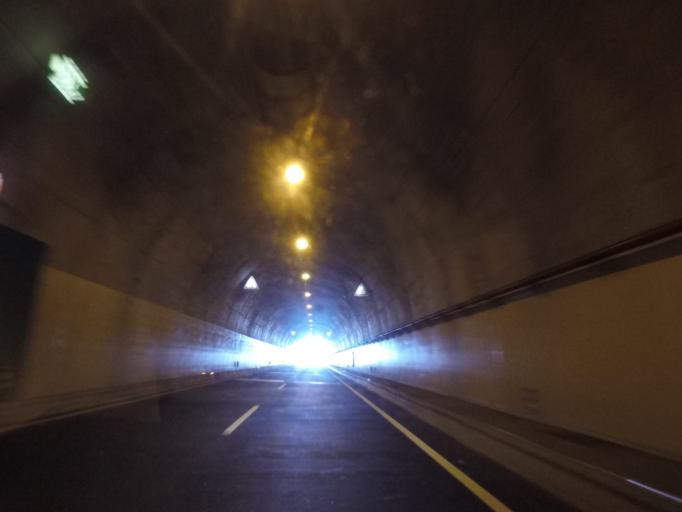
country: PT
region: Madeira
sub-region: Machico
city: Canical
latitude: 32.7434
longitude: -16.7382
